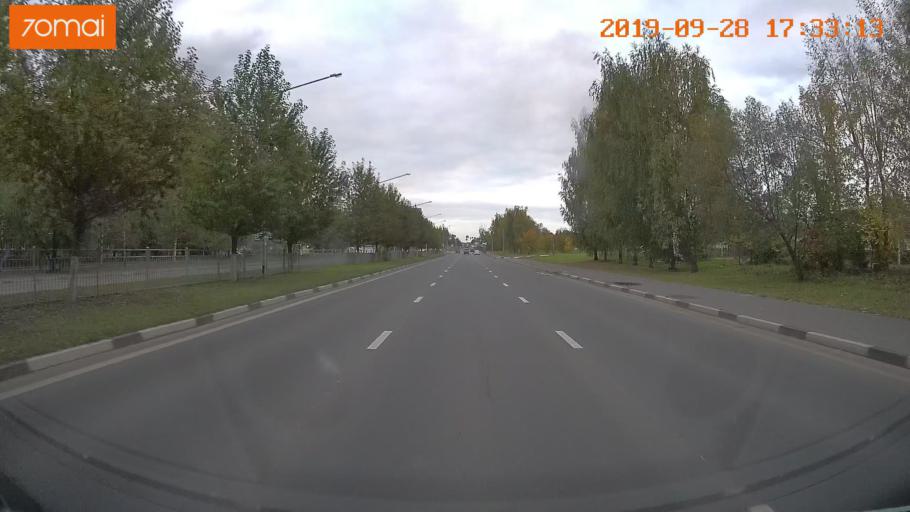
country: RU
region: Jaroslavl
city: Yaroslavl
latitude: 57.5703
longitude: 39.9241
